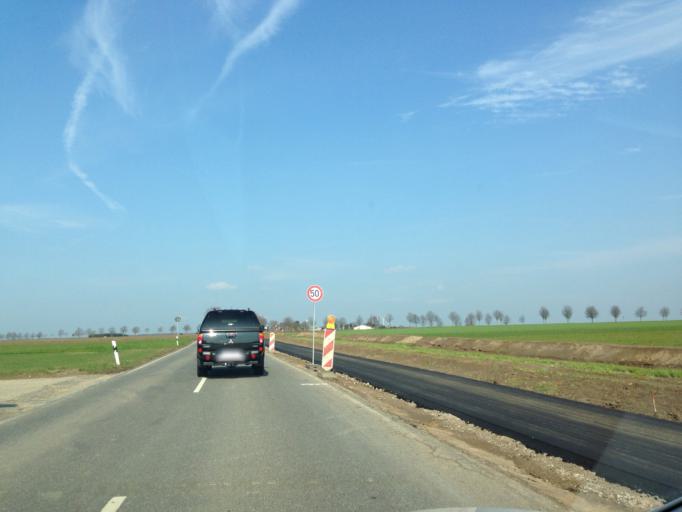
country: DE
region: North Rhine-Westphalia
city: Huckelhoven
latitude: 51.0882
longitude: 6.2457
